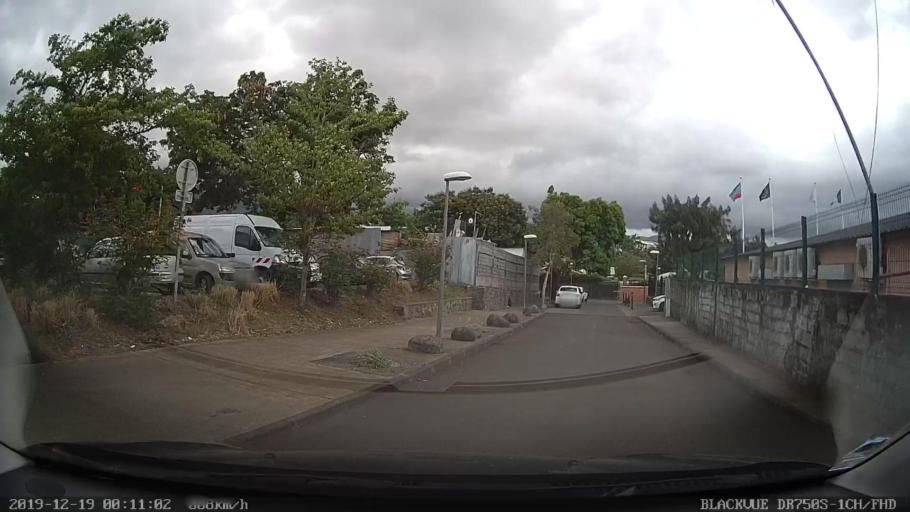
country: RE
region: Reunion
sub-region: Reunion
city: Sainte-Marie
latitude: -20.8995
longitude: 55.5033
